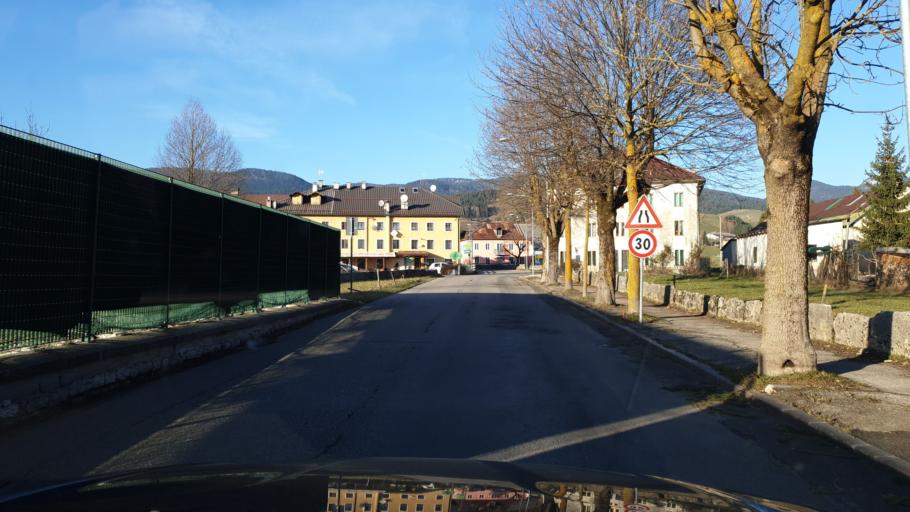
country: IT
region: Veneto
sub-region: Provincia di Vicenza
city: Asiago
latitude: 45.8801
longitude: 11.5097
